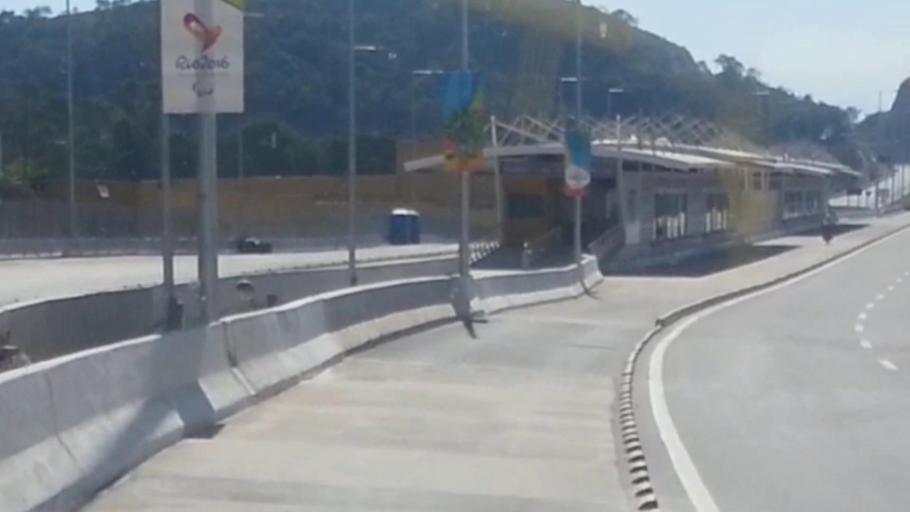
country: BR
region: Rio de Janeiro
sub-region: Nilopolis
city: Nilopolis
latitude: -22.8893
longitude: -43.4010
